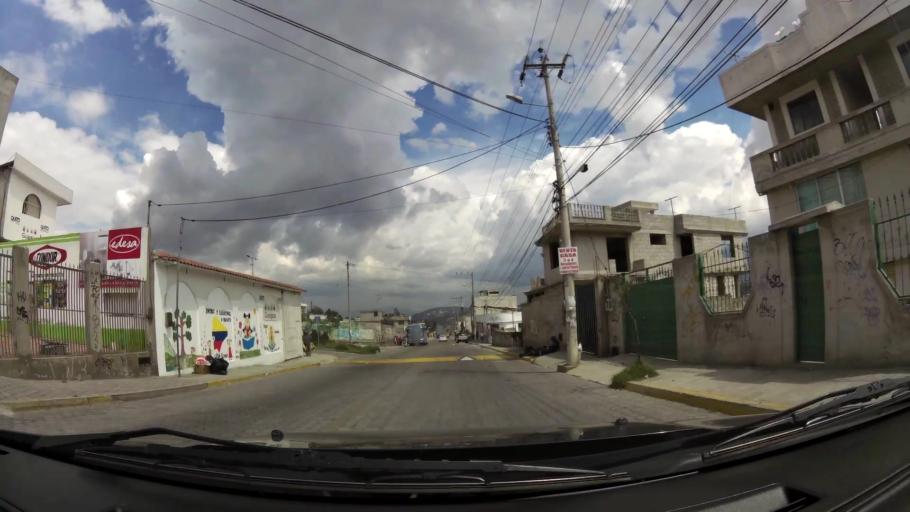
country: EC
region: Pichincha
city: Quito
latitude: -0.0753
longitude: -78.4349
